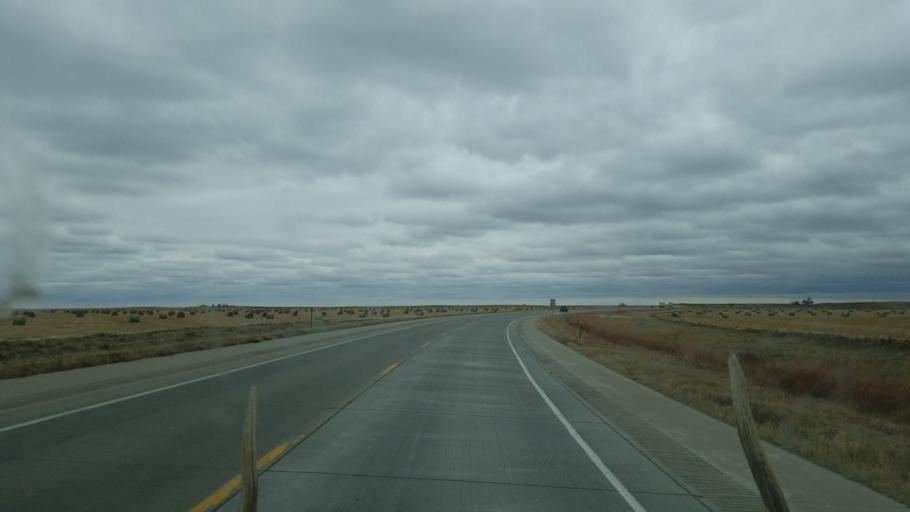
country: US
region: Colorado
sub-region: Kiowa County
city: Eads
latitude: 38.6804
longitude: -102.7848
